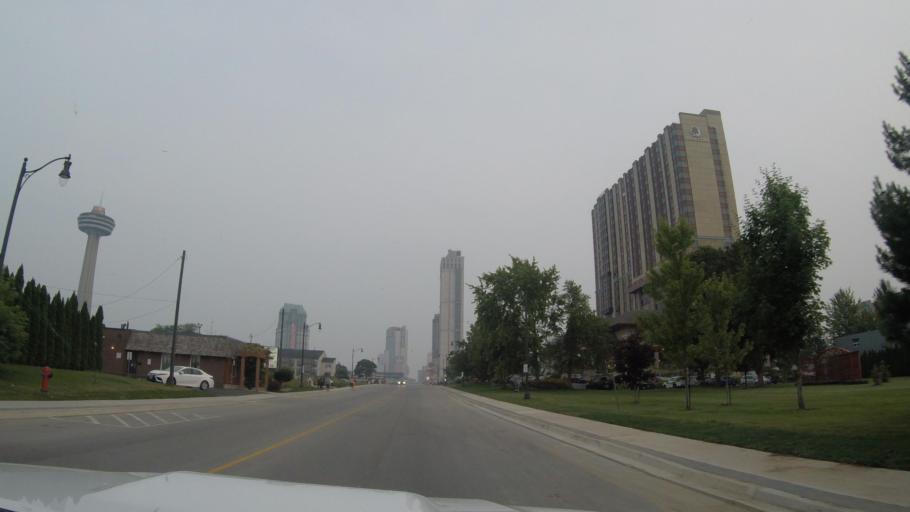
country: CA
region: Ontario
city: Niagara Falls
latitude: 43.0885
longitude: -79.0834
